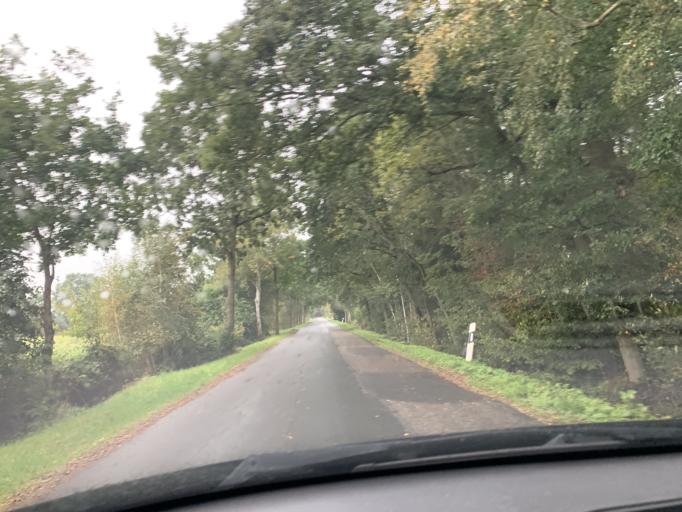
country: DE
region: Lower Saxony
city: Bad Zwischenahn
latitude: 53.1431
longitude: 8.0793
